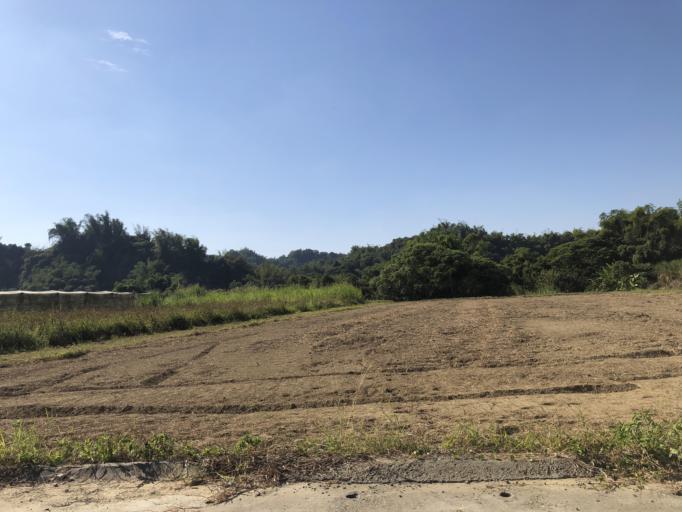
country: TW
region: Taiwan
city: Yujing
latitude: 23.0457
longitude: 120.4012
